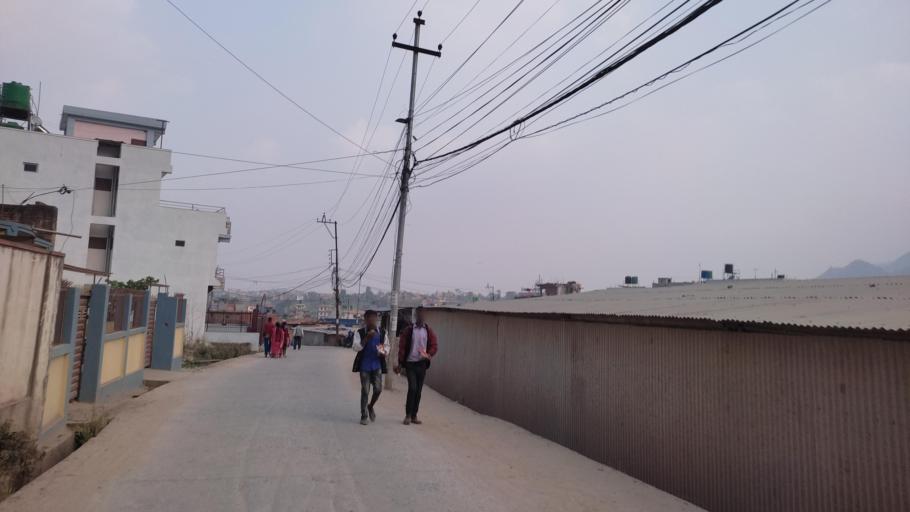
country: NP
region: Central Region
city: Kirtipur
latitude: 27.6826
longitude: 85.2573
